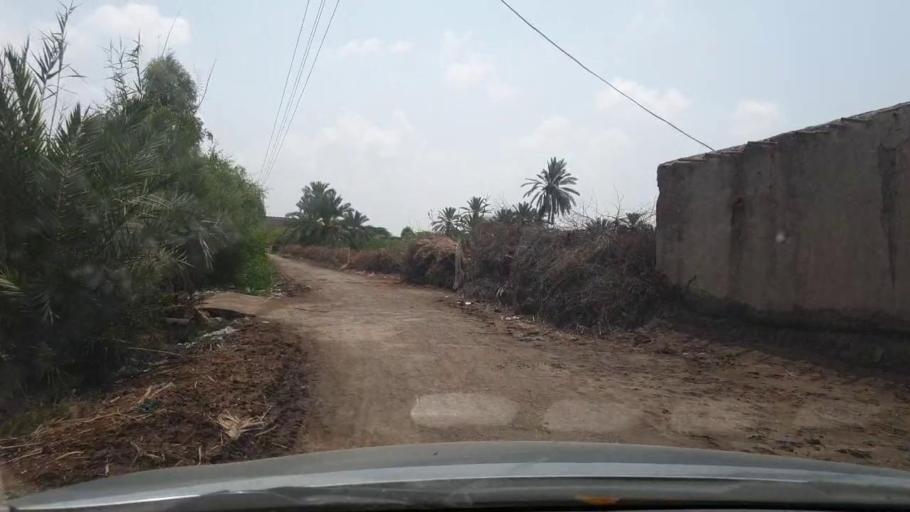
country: PK
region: Sindh
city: Khairpur
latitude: 27.4777
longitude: 68.6913
